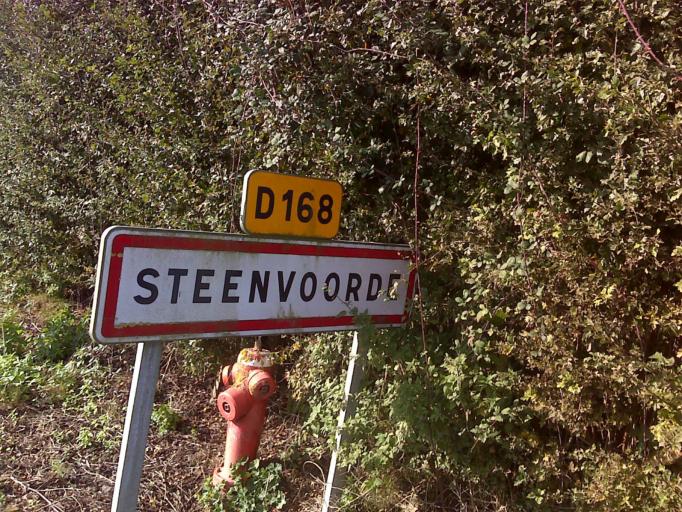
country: FR
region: Nord-Pas-de-Calais
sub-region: Departement du Nord
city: Steenvoorde
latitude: 50.8138
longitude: 2.5990
